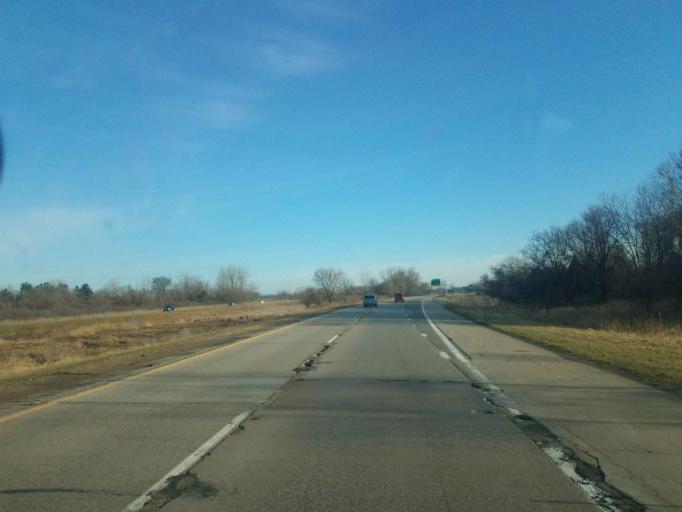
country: US
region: Michigan
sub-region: Ingham County
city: East Lansing
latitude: 42.7895
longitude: -84.5136
